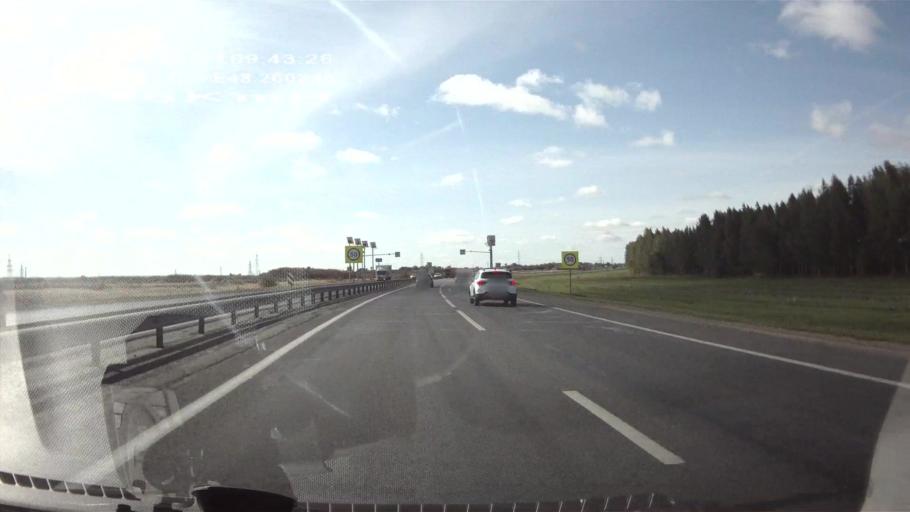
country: RU
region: Ulyanovsk
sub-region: Ulyanovskiy Rayon
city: Ulyanovsk
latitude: 54.2710
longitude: 48.2608
